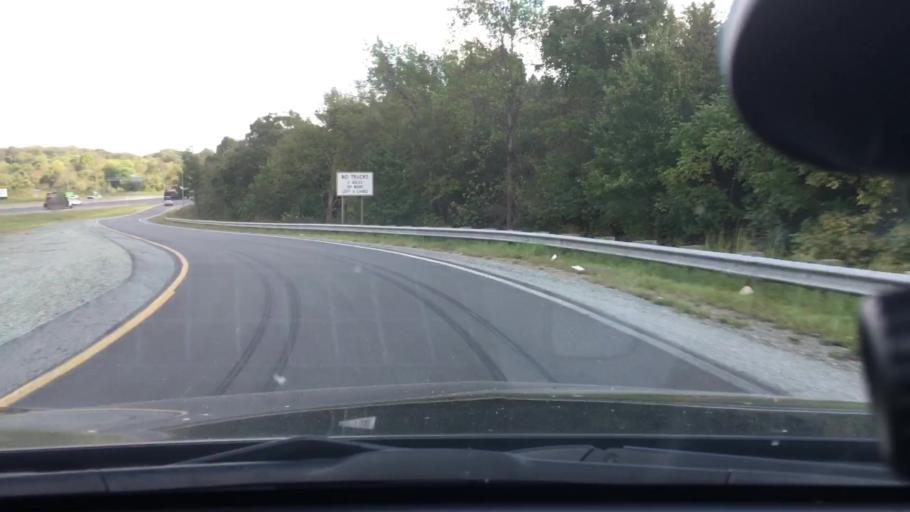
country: US
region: North Carolina
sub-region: Guilford County
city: Gibsonville
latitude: 36.0611
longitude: -79.5664
